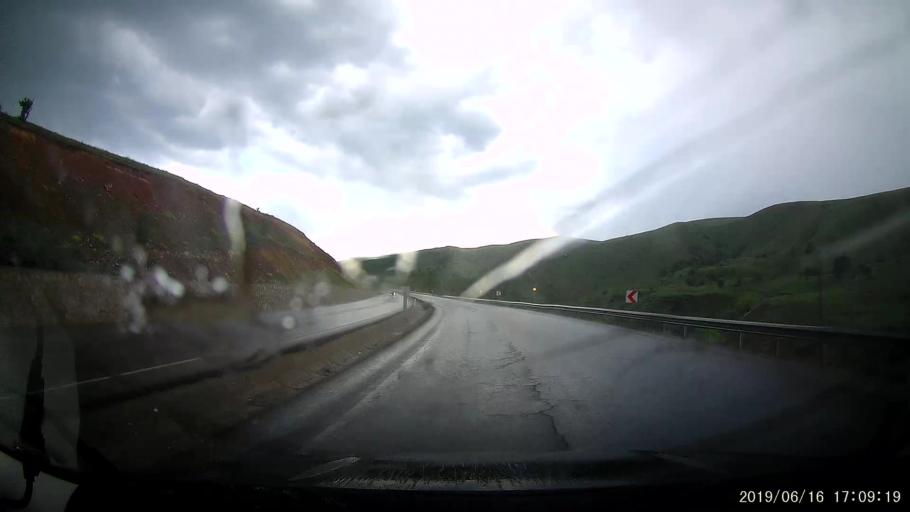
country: TR
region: Erzurum
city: Askale
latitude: 39.8968
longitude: 40.6505
